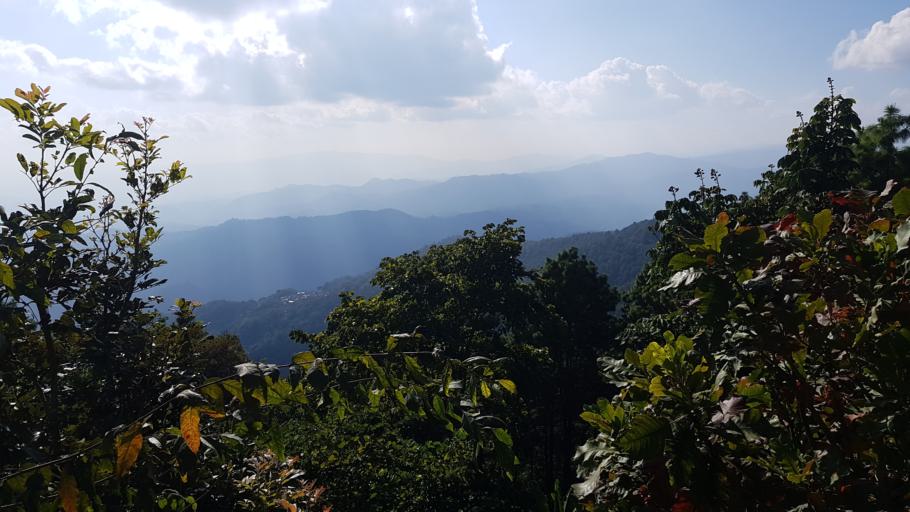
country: TH
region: Chiang Rai
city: Mae Fa Luang
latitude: 20.3351
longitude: 99.8110
